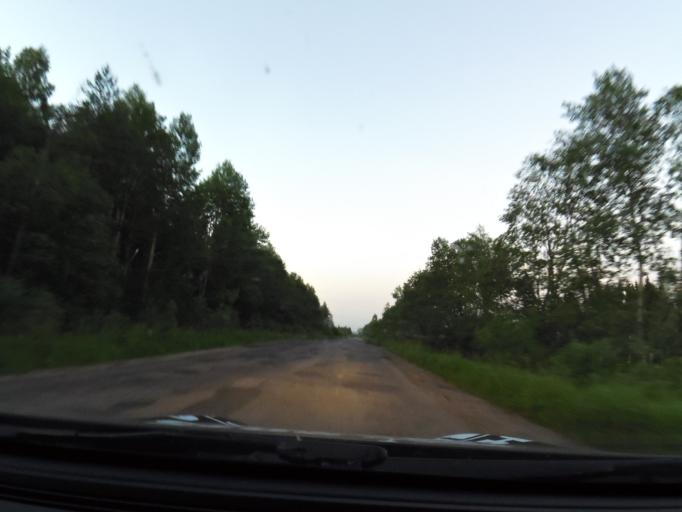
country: RU
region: Kostroma
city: Buy
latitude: 58.4820
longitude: 41.4739
